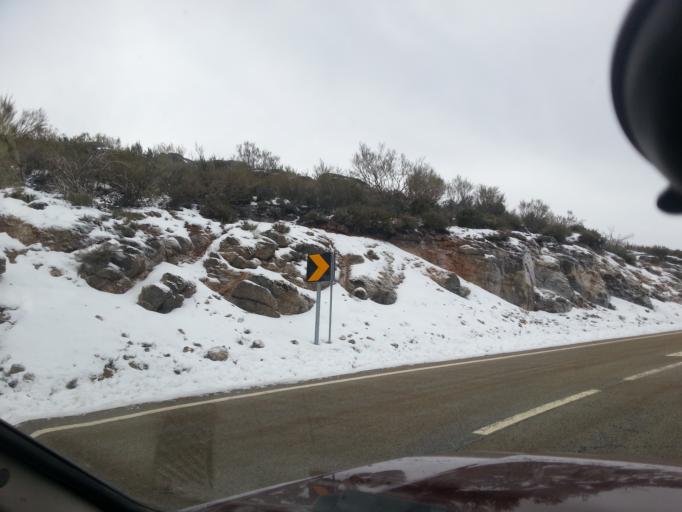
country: PT
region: Guarda
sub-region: Seia
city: Seia
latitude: 40.3562
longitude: -7.6656
